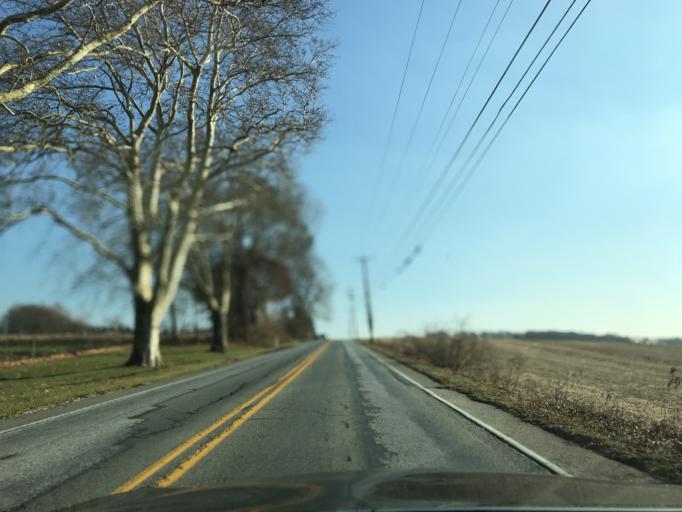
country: US
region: Pennsylvania
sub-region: York County
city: Shrewsbury
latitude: 39.8140
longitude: -76.6866
